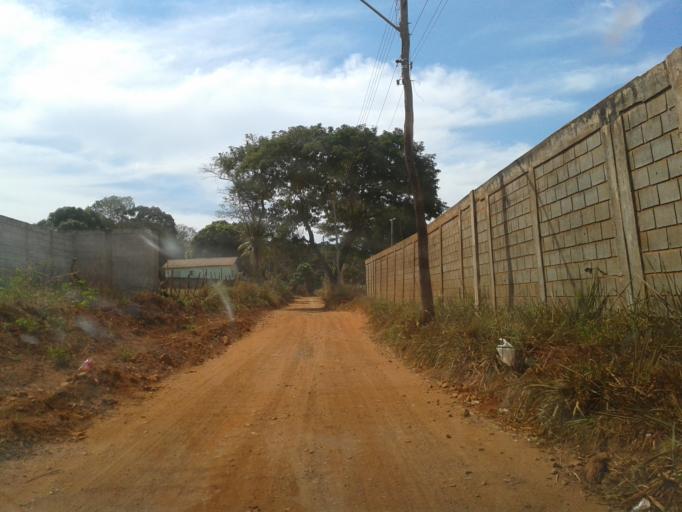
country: BR
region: Goias
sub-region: Goiania
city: Goiania
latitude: -16.6426
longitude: -49.3470
